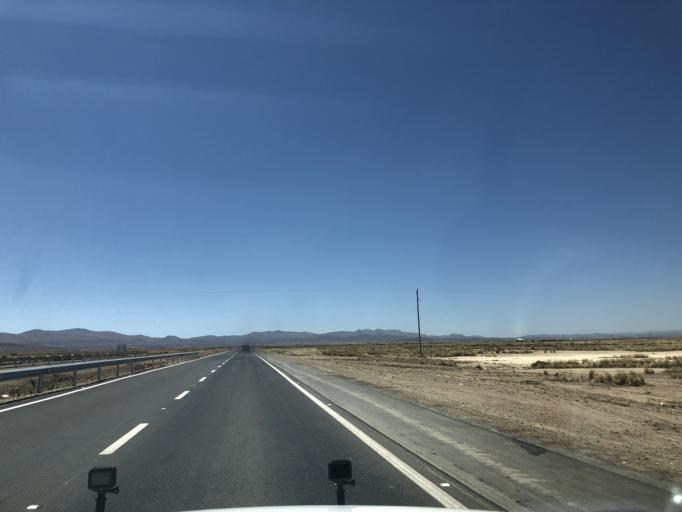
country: BO
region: La Paz
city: Colquiri
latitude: -17.6494
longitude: -67.1985
